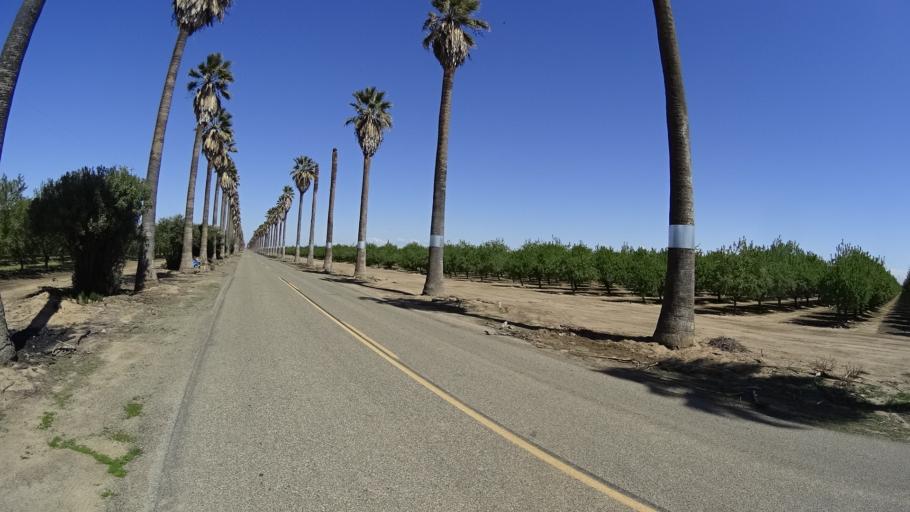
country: US
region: California
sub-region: Fresno County
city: West Park
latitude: 36.7068
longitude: -119.9345
